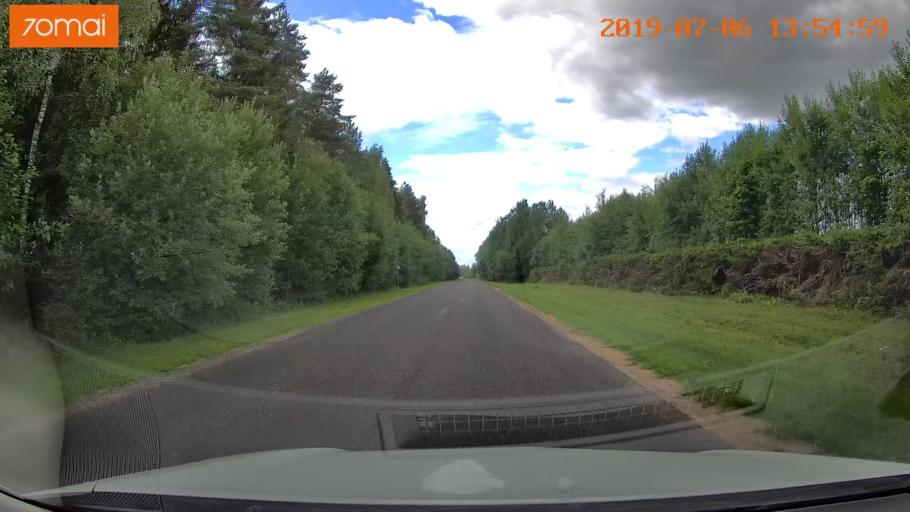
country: BY
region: Minsk
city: Ivyanyets
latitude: 53.7512
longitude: 26.8140
